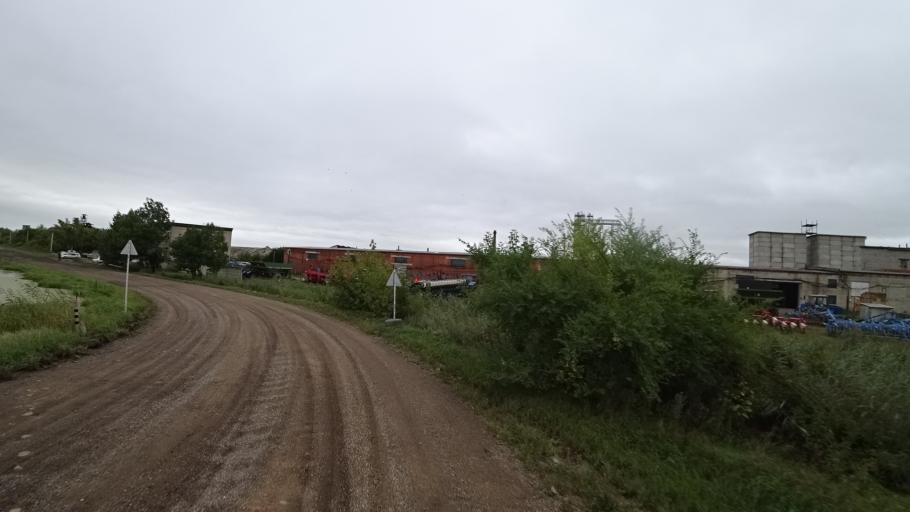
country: RU
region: Primorskiy
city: Chernigovka
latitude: 44.3330
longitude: 132.5238
